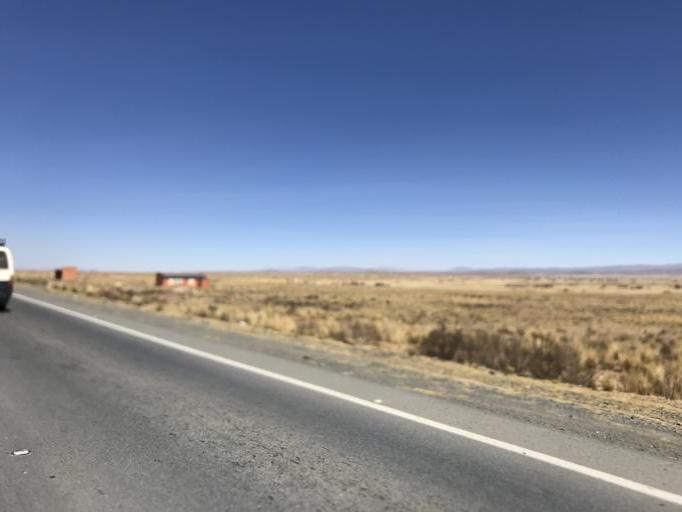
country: BO
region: La Paz
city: Batallas
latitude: -16.4007
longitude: -68.3590
